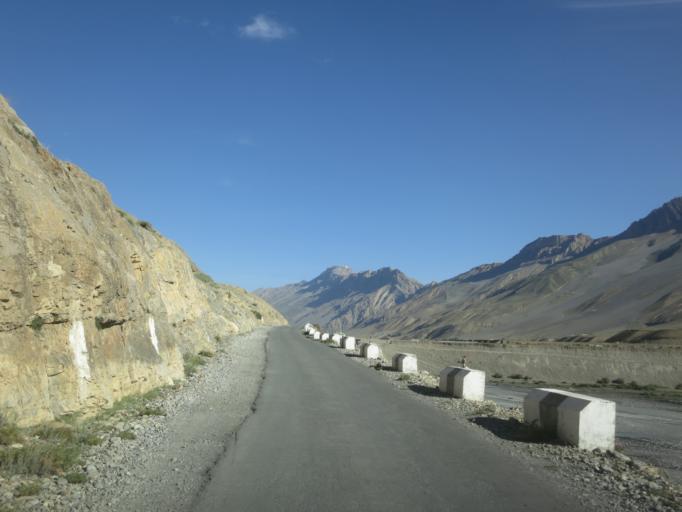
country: IN
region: Himachal Pradesh
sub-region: Shimla
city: Sarahan
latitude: 32.2493
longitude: 78.0511
